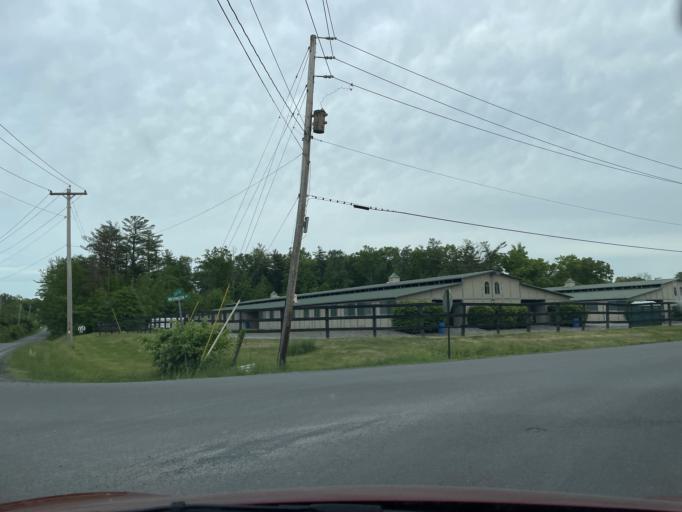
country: US
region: New York
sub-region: Ulster County
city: Saugerties
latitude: 42.0978
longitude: -73.9474
